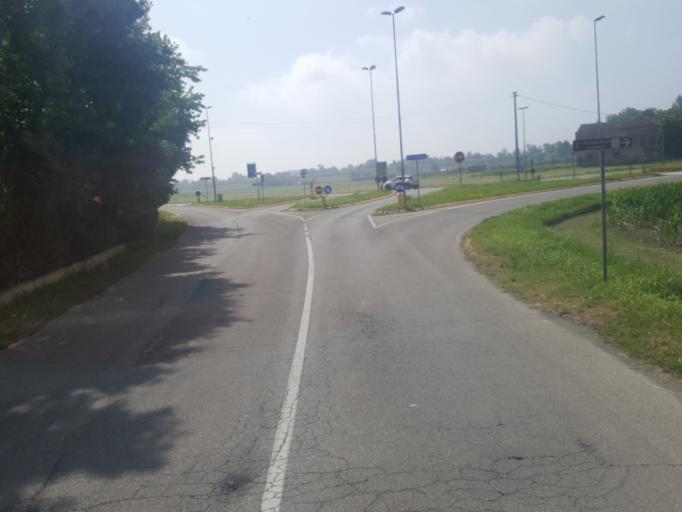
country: IT
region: Veneto
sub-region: Provincia di Rovigo
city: Canaro
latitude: 44.9260
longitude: 11.6884
